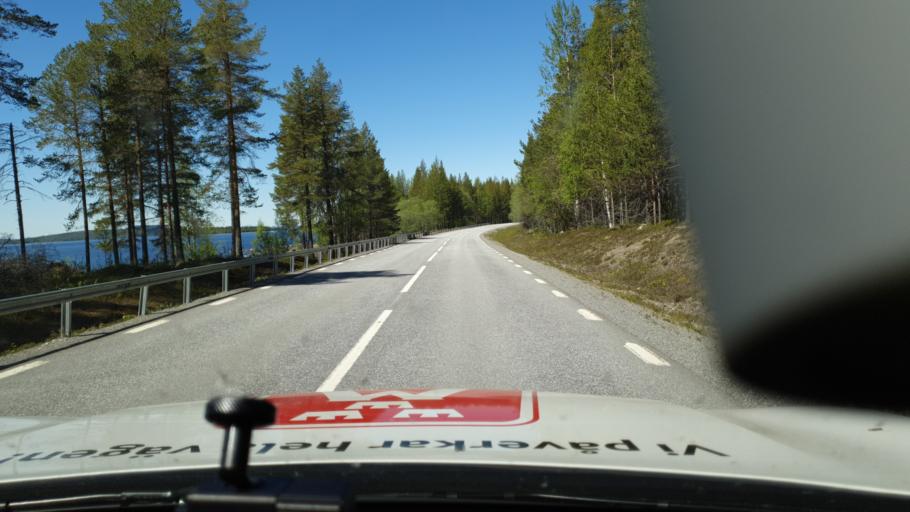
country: SE
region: Vaesterbotten
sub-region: Storumans Kommun
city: Storuman
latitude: 65.1615
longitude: 17.0434
